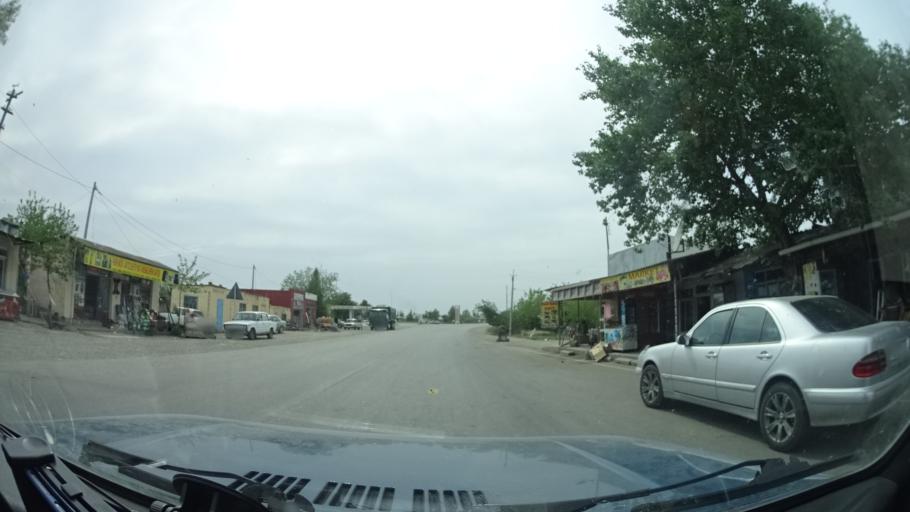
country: IR
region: Ardabil
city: Parsabad
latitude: 39.7352
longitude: 47.9524
